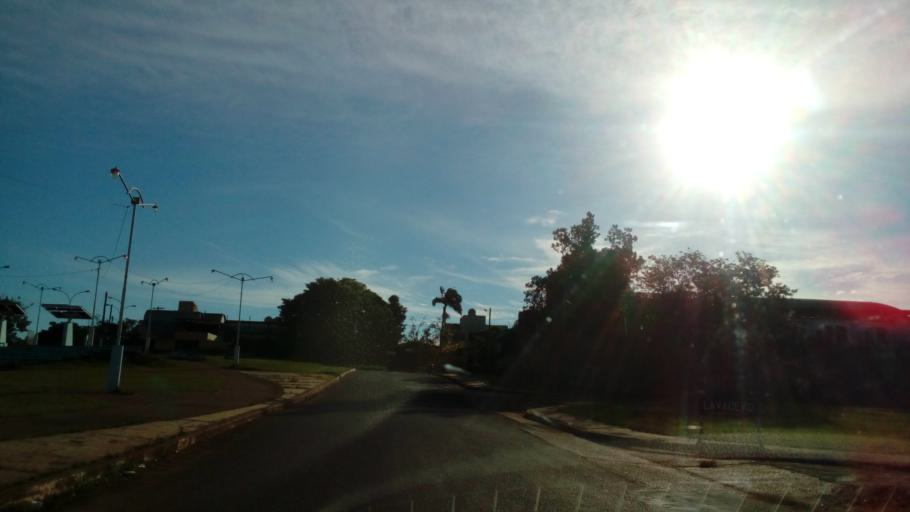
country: AR
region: Misiones
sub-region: Departamento de Capital
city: Posadas
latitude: -27.4273
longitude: -55.8795
